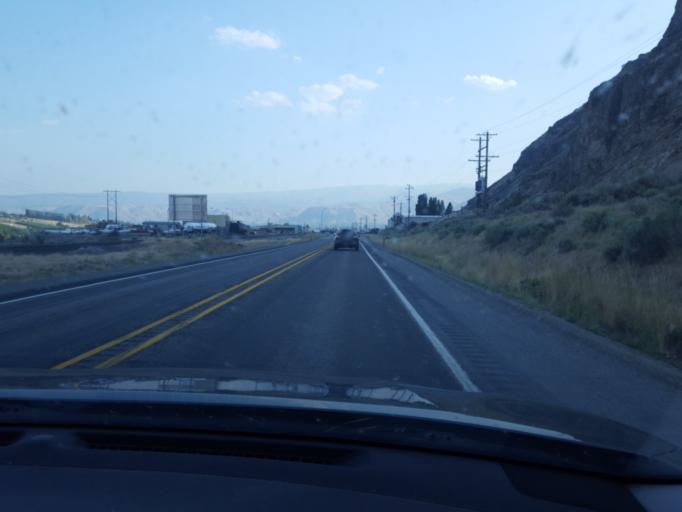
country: US
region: Washington
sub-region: Chelan County
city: Sunnyslope
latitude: 47.4974
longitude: -120.3127
